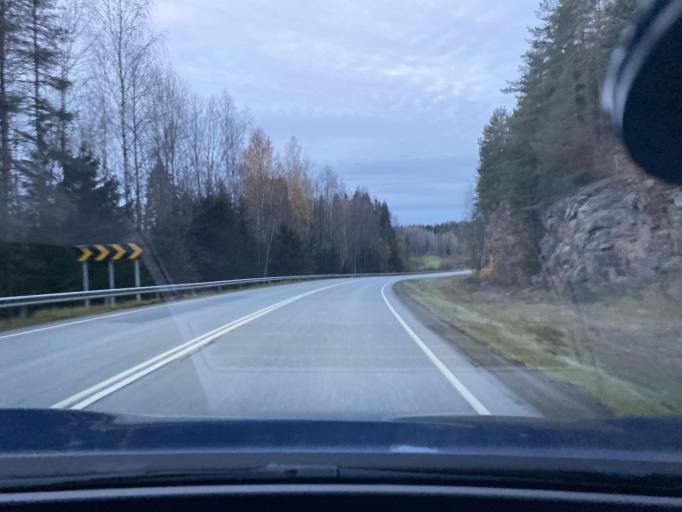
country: FI
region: Uusimaa
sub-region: Helsinki
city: Sammatti
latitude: 60.3885
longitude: 23.8159
